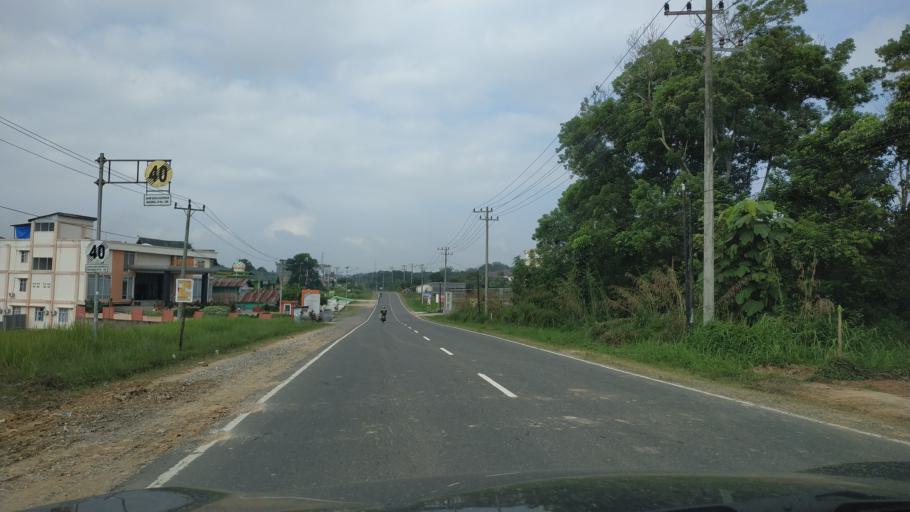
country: ID
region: Riau
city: Rengat
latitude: -0.3935
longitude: 102.4336
